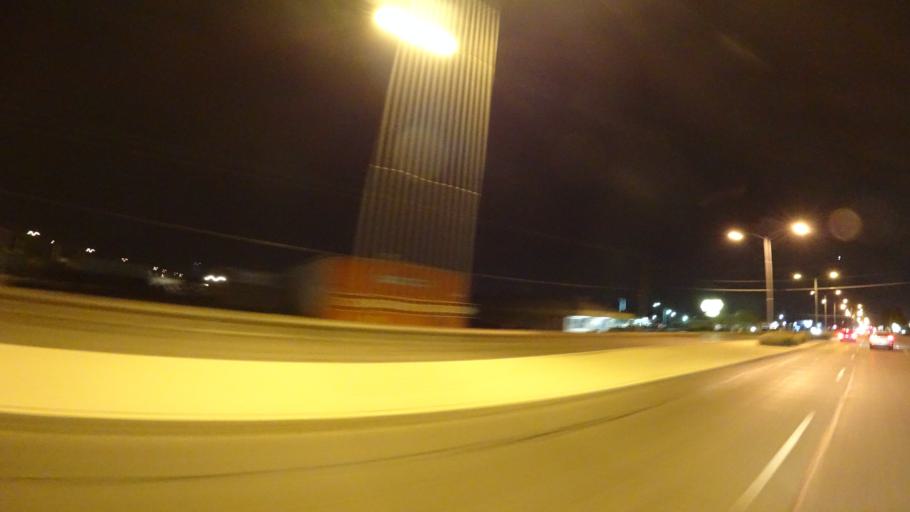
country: US
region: Arizona
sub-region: Maricopa County
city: Gilbert
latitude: 33.4156
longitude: -111.7456
